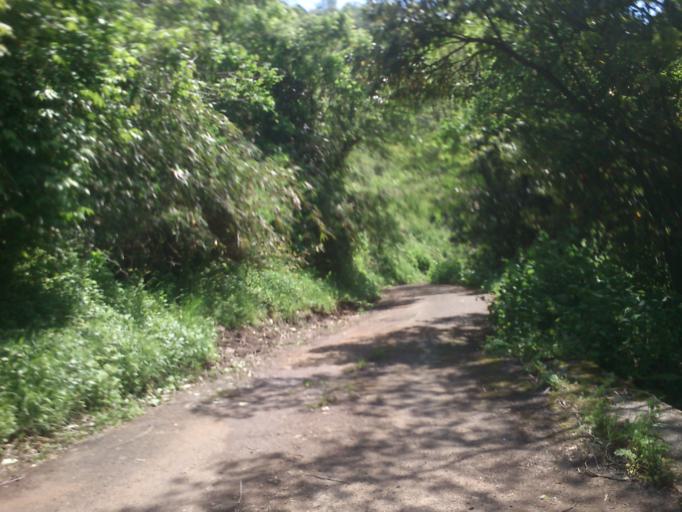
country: JP
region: Kyoto
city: Miyazu
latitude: 35.7157
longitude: 135.1416
